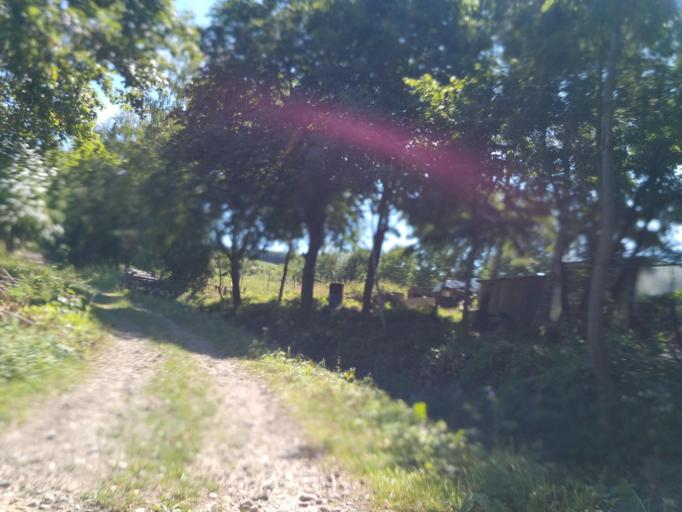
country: PL
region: Subcarpathian Voivodeship
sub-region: Powiat sanocki
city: Bukowsko
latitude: 49.4883
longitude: 22.0684
